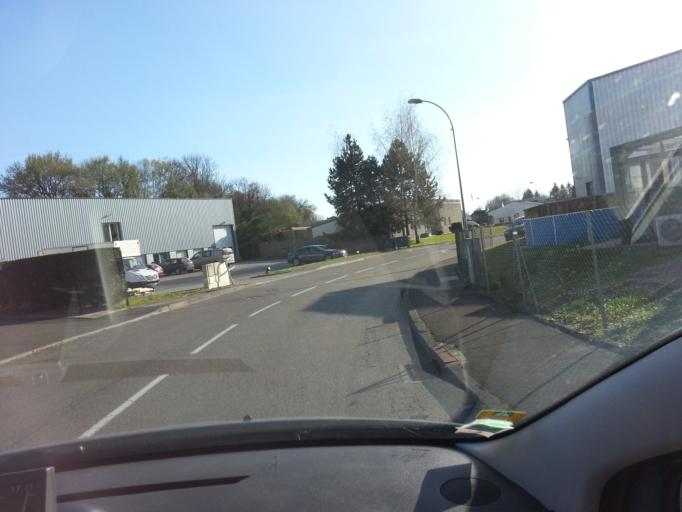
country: FR
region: Franche-Comte
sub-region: Departement du Doubs
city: Miserey-Salines
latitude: 47.2739
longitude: 5.9936
